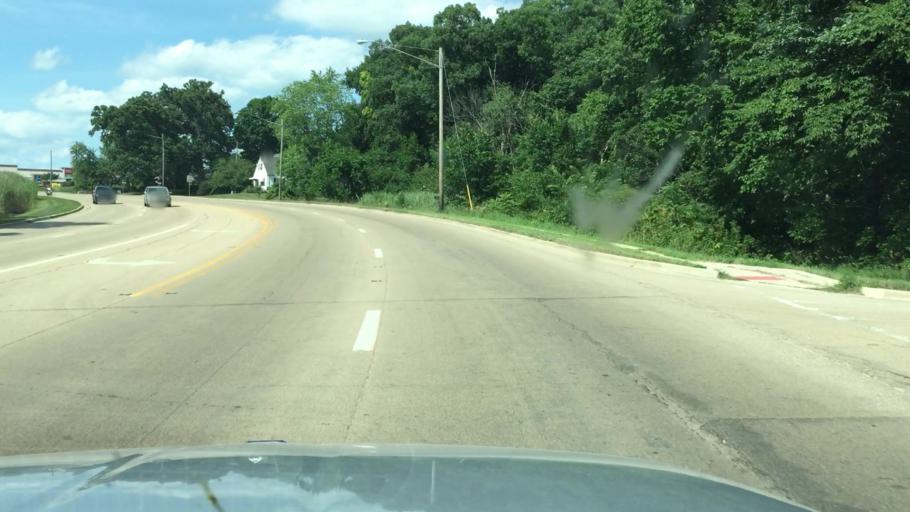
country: US
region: Illinois
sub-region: LaSalle County
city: Ottawa
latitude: 41.3674
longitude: -88.8358
